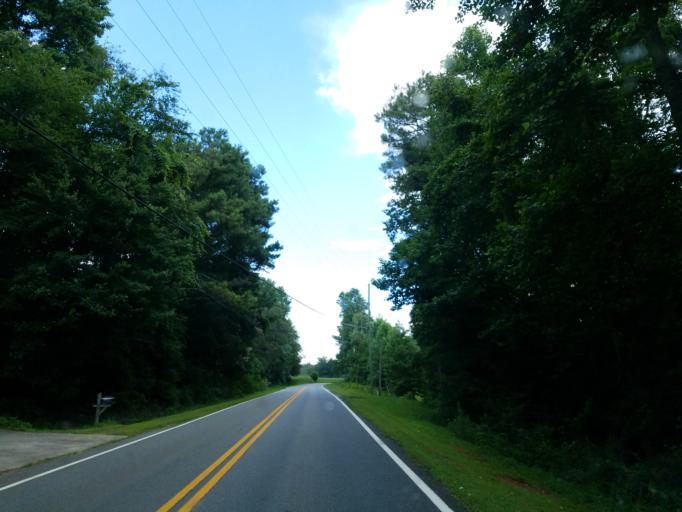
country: US
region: Georgia
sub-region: Gilmer County
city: Ellijay
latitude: 34.6707
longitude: -84.3631
